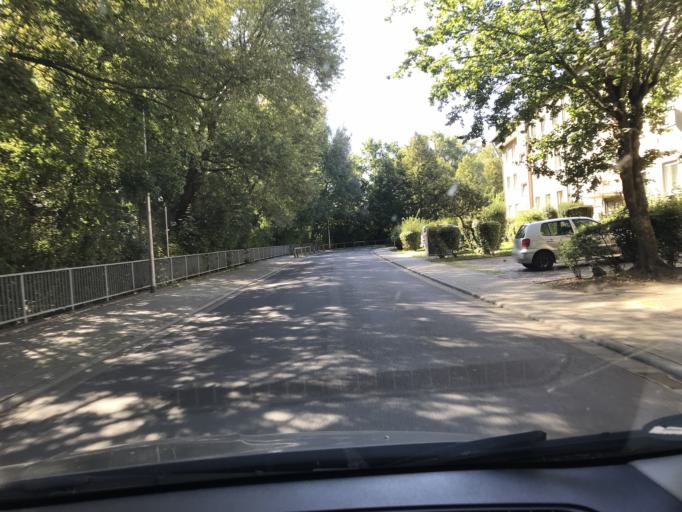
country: DE
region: Hesse
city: Gross-Umstadt
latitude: 49.8762
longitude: 8.9270
